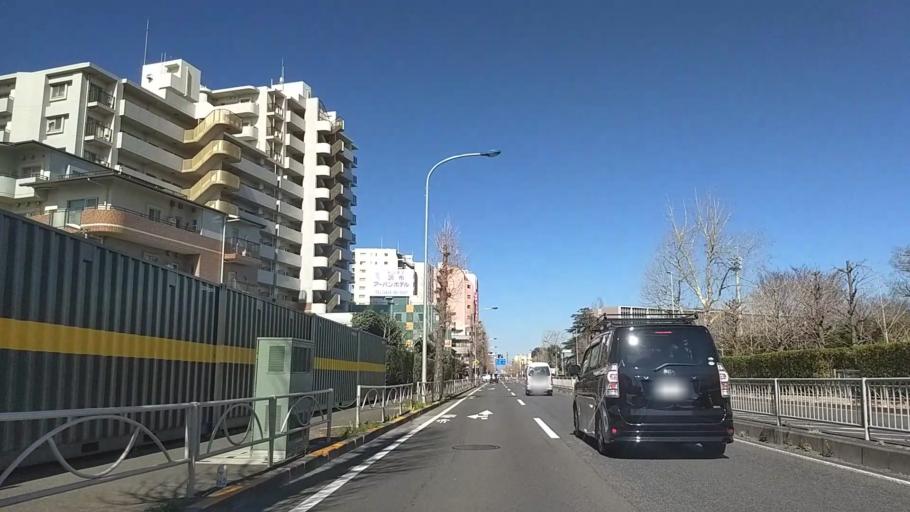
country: JP
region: Tokyo
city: Chofugaoka
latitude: 35.6638
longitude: 139.5236
